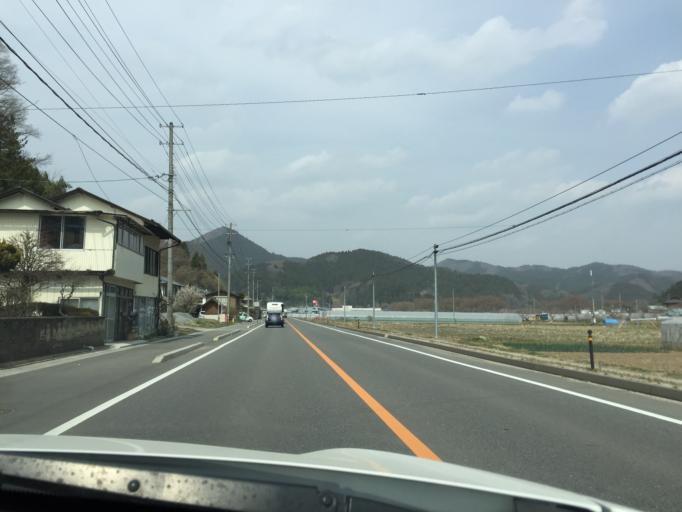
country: JP
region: Fukushima
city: Ishikawa
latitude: 37.0884
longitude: 140.5275
